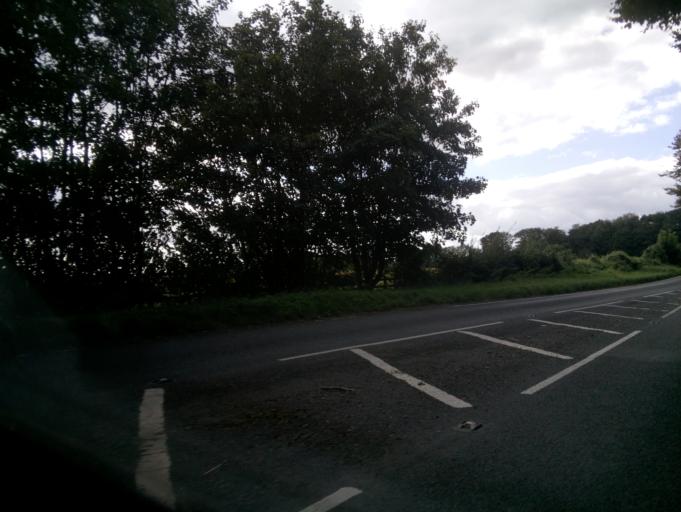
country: GB
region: England
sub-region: Hampshire
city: Chandlers Ford
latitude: 51.1029
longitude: -1.4107
